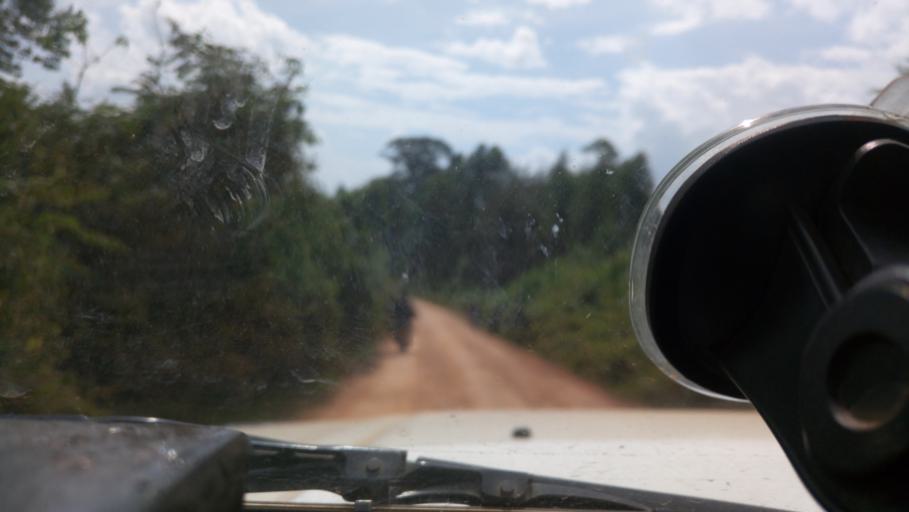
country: KE
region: Kericho
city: Litein
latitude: -0.5786
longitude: 35.1088
